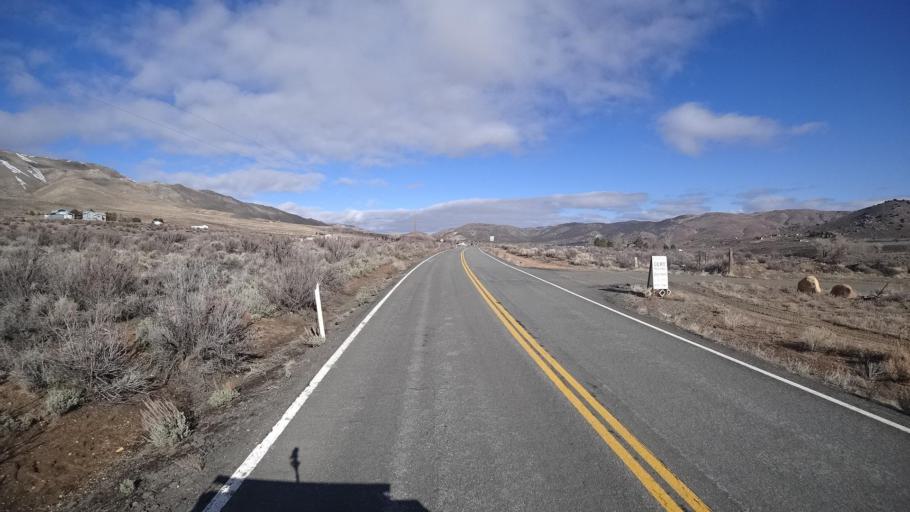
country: US
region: Nevada
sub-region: Washoe County
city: Cold Springs
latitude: 39.8700
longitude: -119.9612
